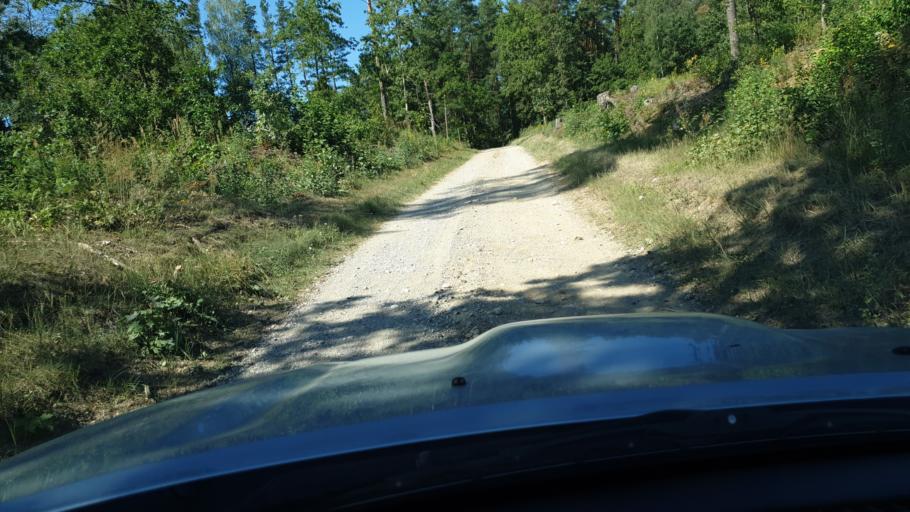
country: LT
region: Vilnius County
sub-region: Vilniaus Rajonas
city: Vievis
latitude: 54.9027
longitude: 24.8817
